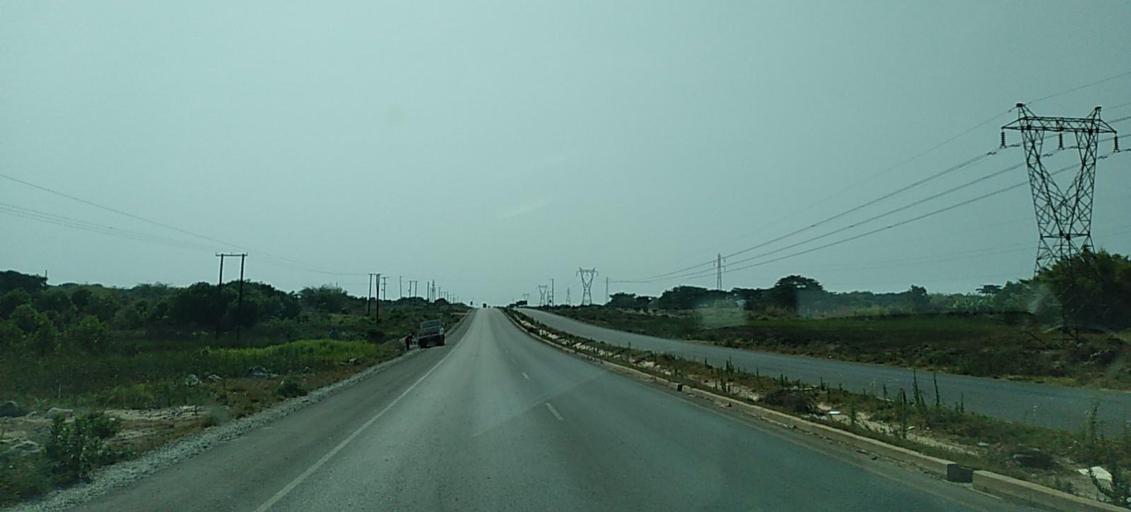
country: ZM
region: Copperbelt
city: Chingola
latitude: -12.5651
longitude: 27.8913
